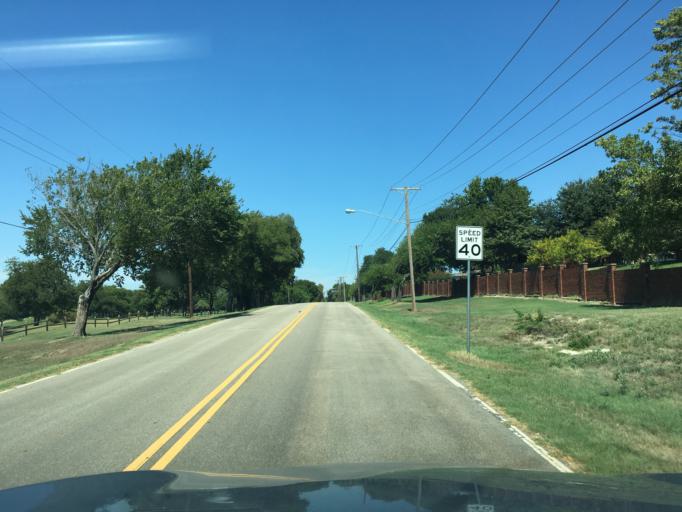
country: US
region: Texas
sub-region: Dallas County
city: Sachse
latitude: 32.9699
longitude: -96.6210
